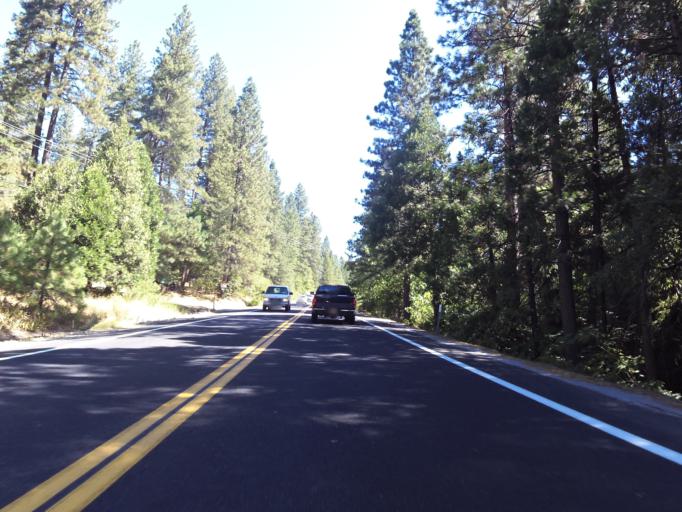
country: US
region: California
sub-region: Calaveras County
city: Forest Meadows
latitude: 38.1678
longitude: -120.4153
